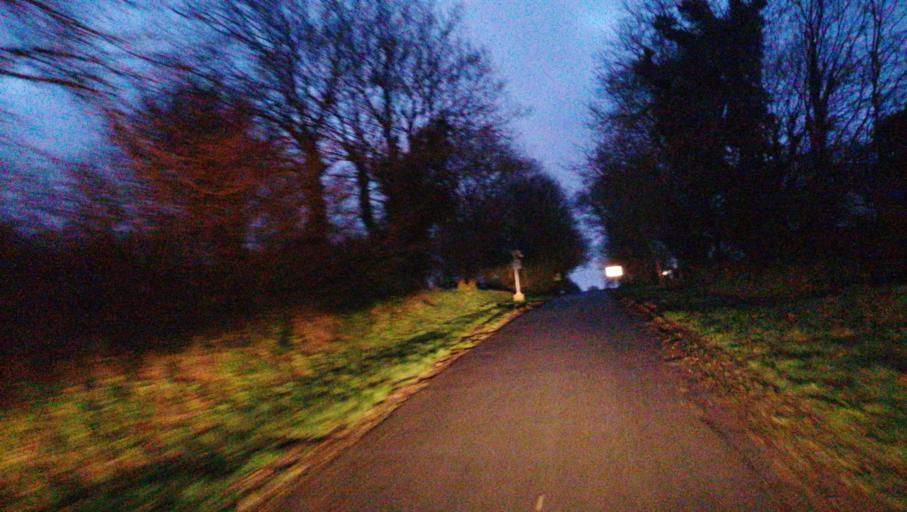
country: FR
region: Brittany
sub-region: Departement des Cotes-d'Armor
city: Plehedel
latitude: 48.6780
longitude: -3.0402
